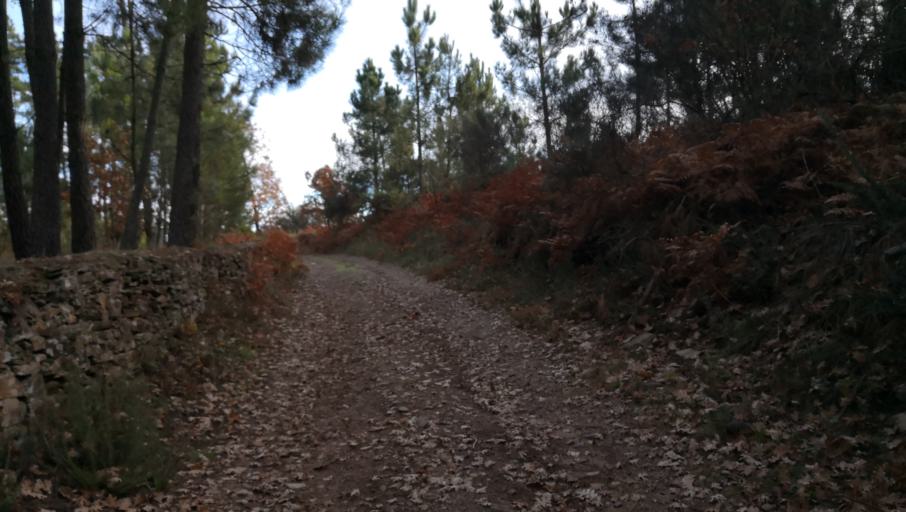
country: PT
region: Vila Real
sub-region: Sabrosa
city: Vilela
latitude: 41.2535
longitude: -7.6326
